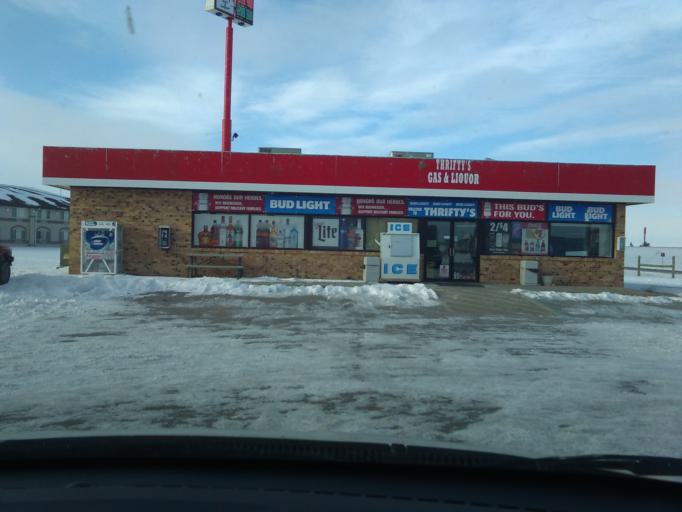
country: US
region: Nebraska
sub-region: Cheyenne County
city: Sidney
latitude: 41.1112
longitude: -102.9504
